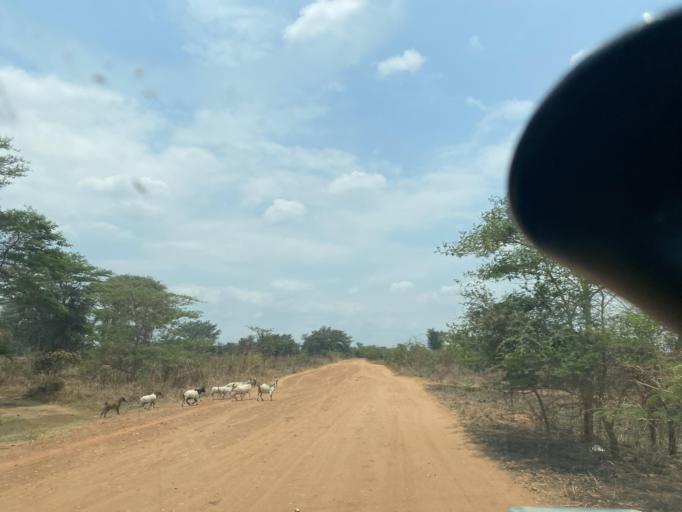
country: ZM
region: Lusaka
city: Chongwe
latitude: -15.5178
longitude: 28.8206
